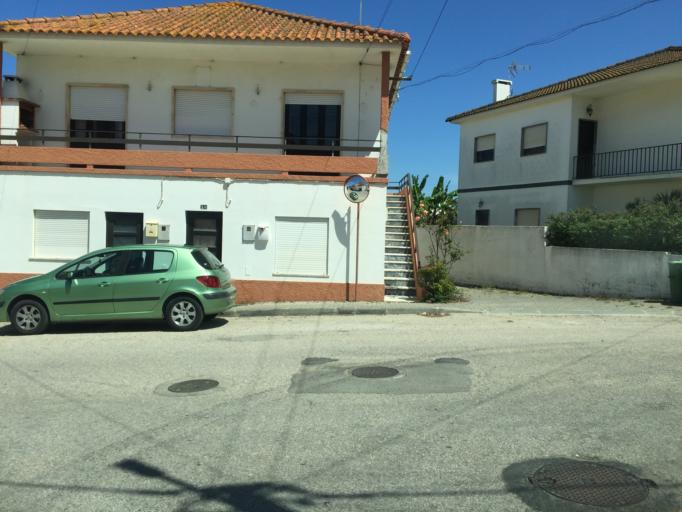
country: PT
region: Lisbon
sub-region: Lourinha
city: Lourinha
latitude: 39.2030
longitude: -9.3306
